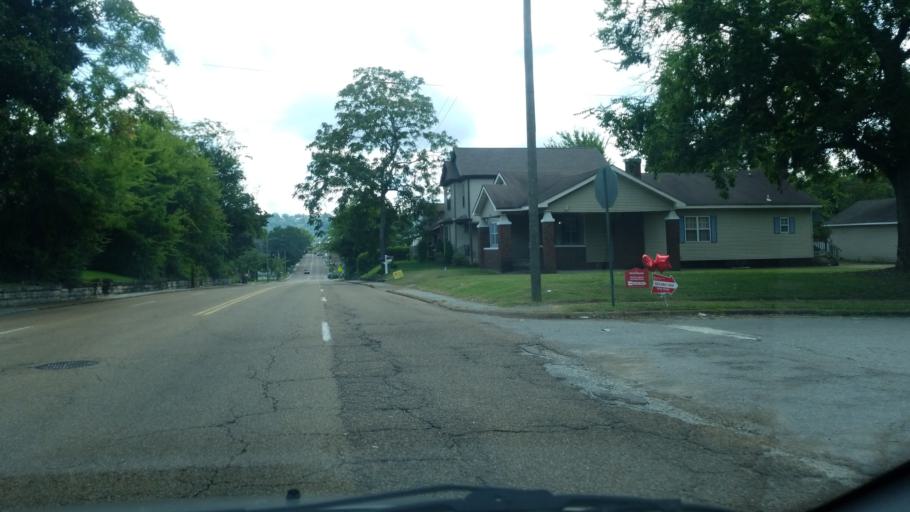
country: US
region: Tennessee
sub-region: Hamilton County
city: Chattanooga
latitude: 35.0350
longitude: -85.2803
